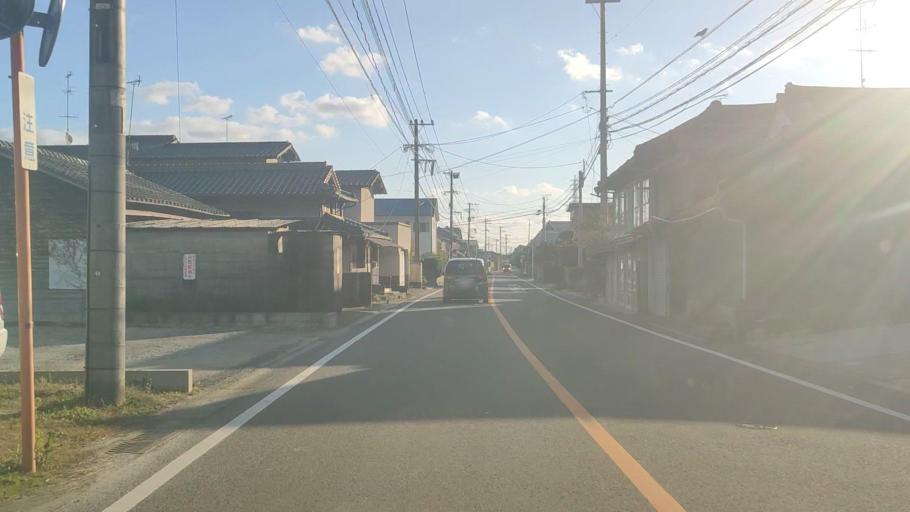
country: JP
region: Saga Prefecture
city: Saga-shi
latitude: 33.3243
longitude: 130.2681
